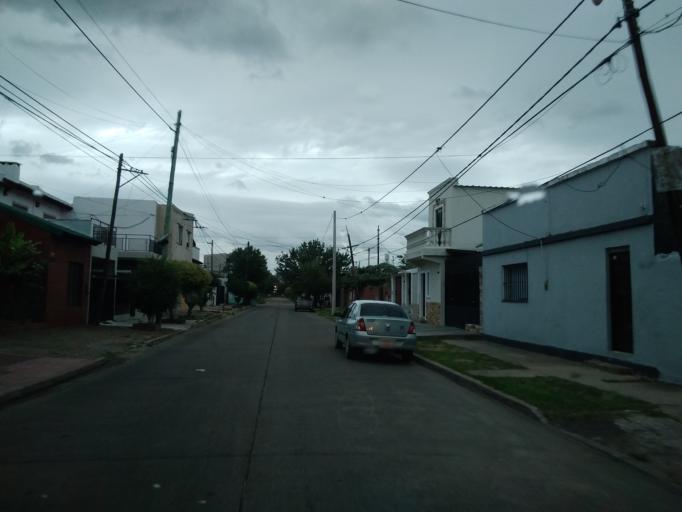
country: AR
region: Corrientes
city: Corrientes
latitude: -27.4788
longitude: -58.8253
